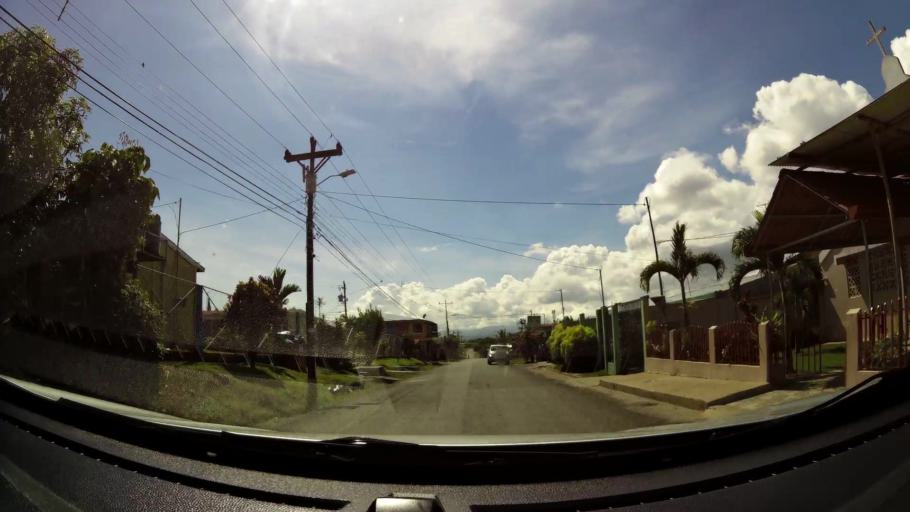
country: CR
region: San Jose
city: San Isidro
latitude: 9.3836
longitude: -83.6978
